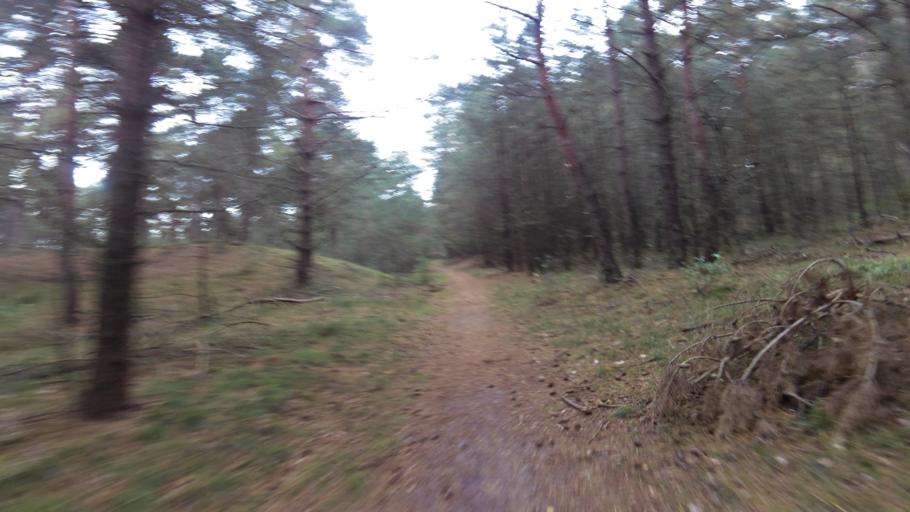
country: NL
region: Gelderland
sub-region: Gemeente Barneveld
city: Stroe
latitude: 52.1713
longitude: 5.7311
